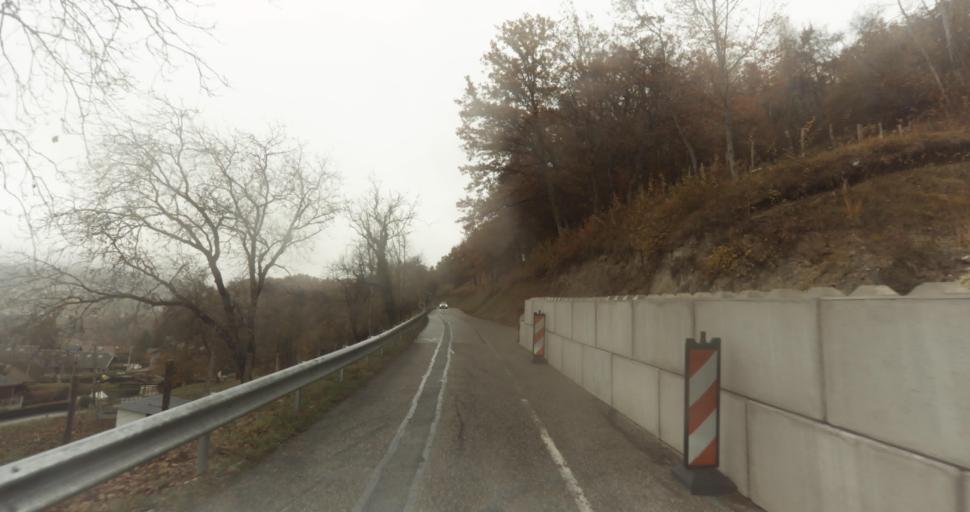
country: FR
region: Rhone-Alpes
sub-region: Departement de la Haute-Savoie
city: Villaz
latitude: 45.9404
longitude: 6.1701
